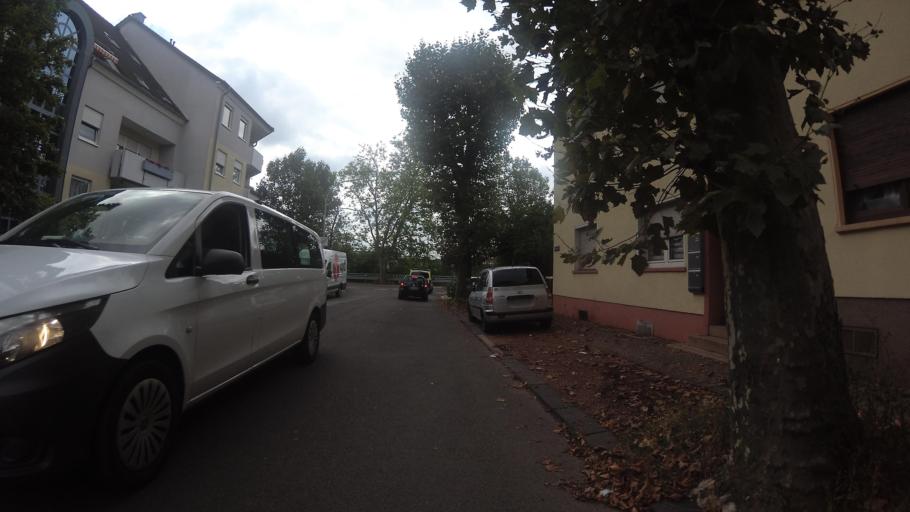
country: DE
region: Saarland
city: Saarbrucken
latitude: 49.2424
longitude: 6.9599
